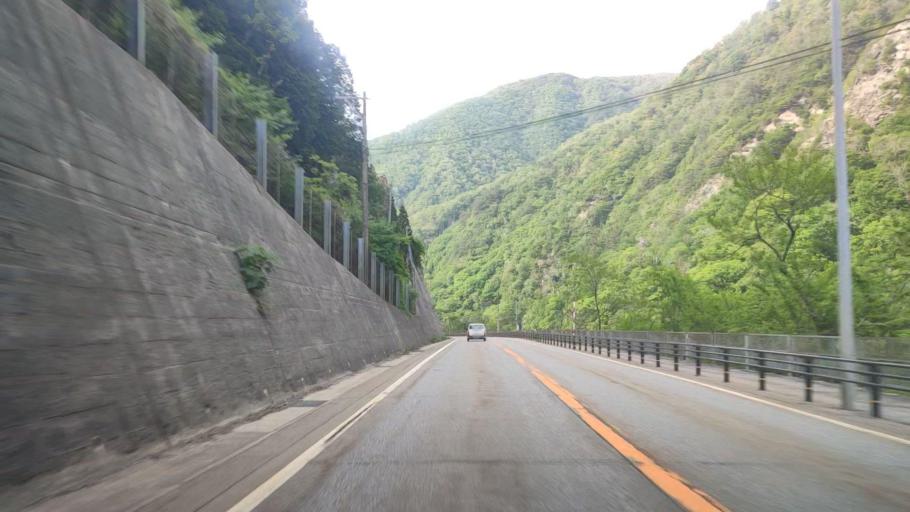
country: JP
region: Gifu
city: Takayama
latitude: 36.3547
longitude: 137.2877
